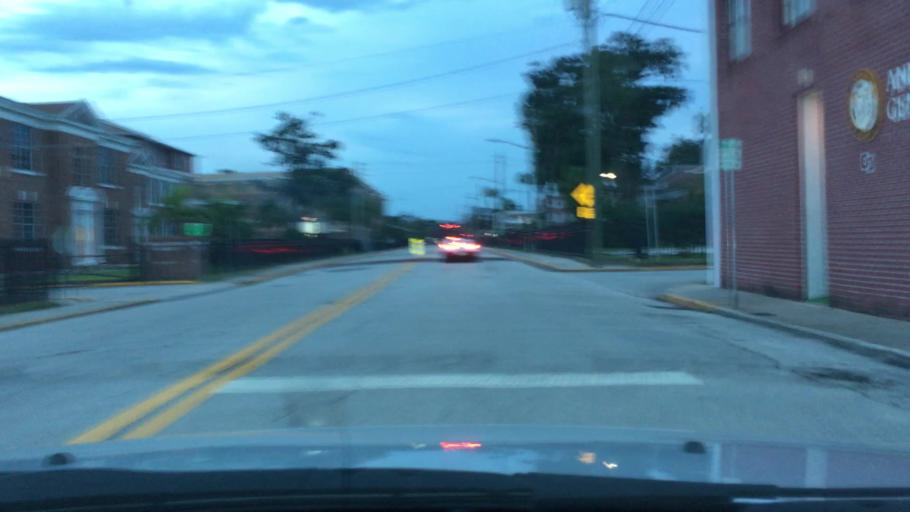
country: US
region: Florida
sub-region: Volusia County
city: Daytona Beach
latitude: 29.2123
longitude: -81.0308
